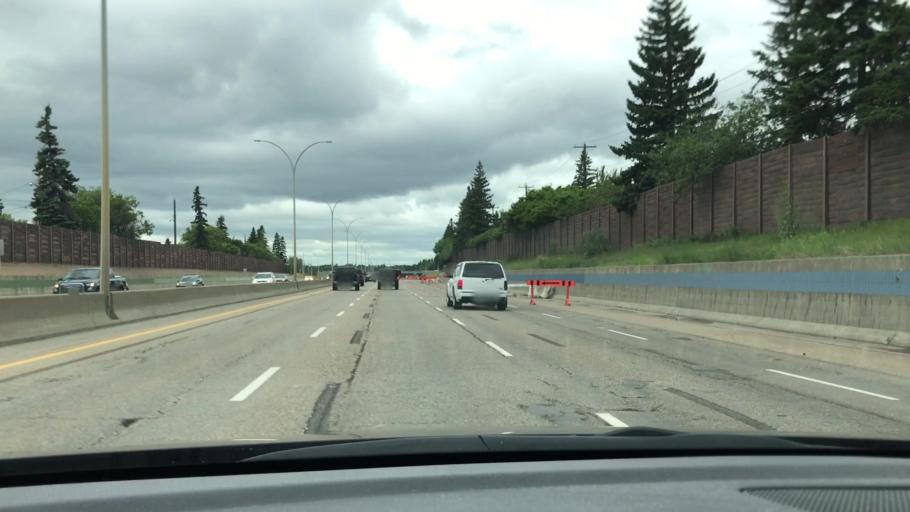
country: CA
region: Alberta
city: Edmonton
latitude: 53.4832
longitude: -113.5331
